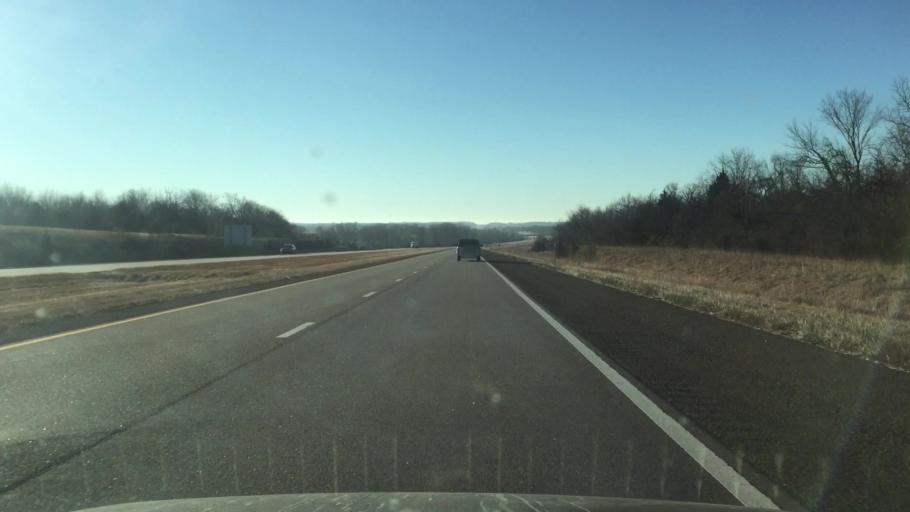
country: US
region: Kansas
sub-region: Johnson County
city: Spring Hill
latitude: 38.7118
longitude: -94.8347
